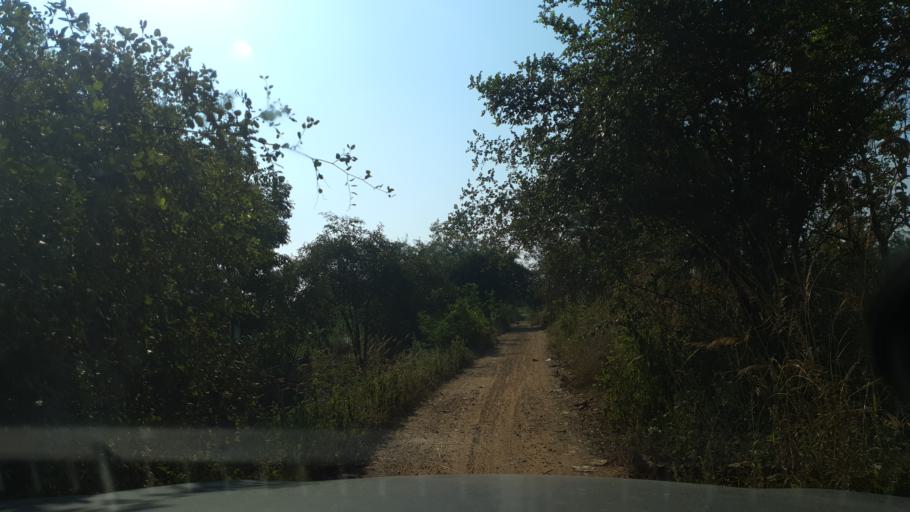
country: TH
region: Lamphun
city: Ban Thi
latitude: 18.6741
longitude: 99.1405
